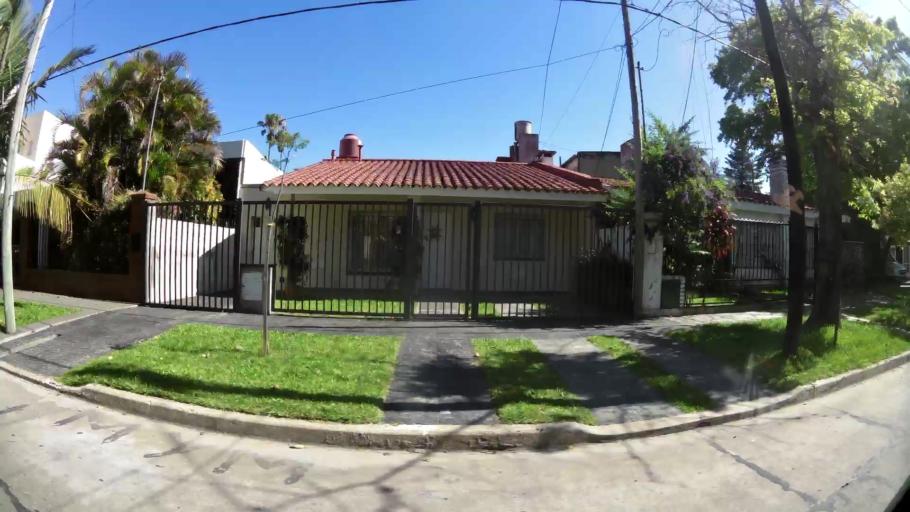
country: AR
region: Santa Fe
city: Santa Fe de la Vera Cruz
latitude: -31.6035
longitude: -60.6686
